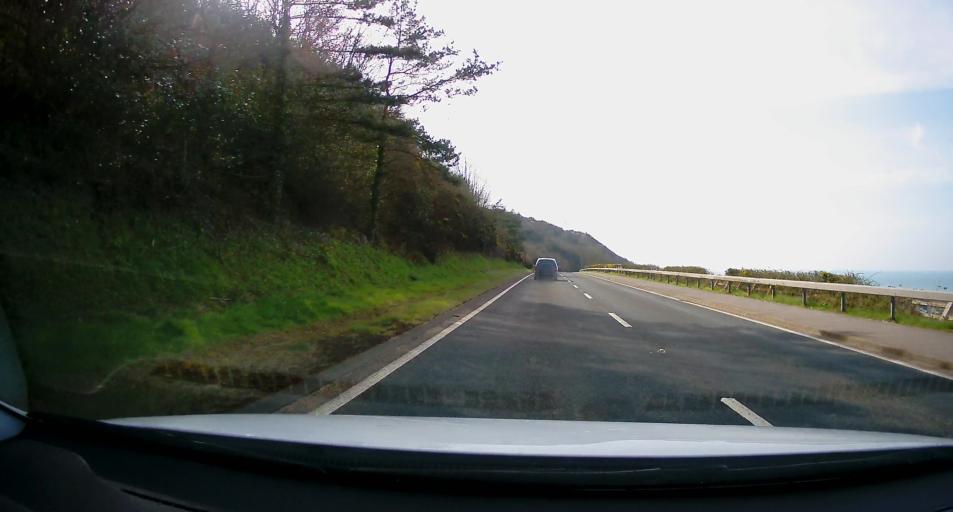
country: GB
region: Wales
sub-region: County of Ceredigion
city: Aberaeron
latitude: 52.2457
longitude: -4.2435
